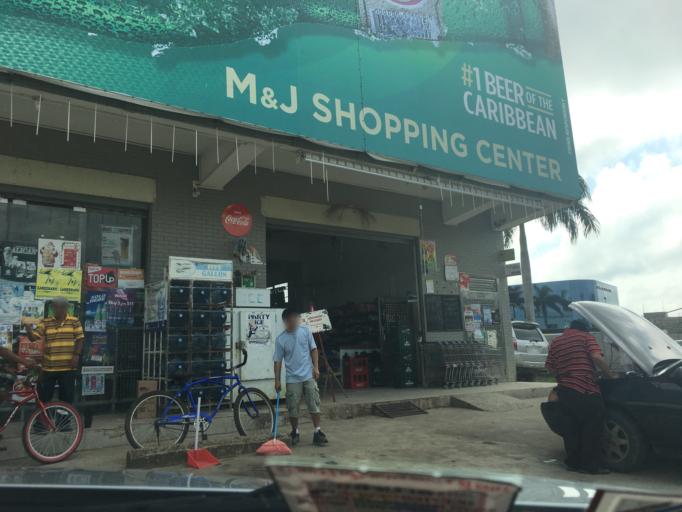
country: BZ
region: Cayo
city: Belmopan
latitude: 17.2557
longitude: -88.7857
